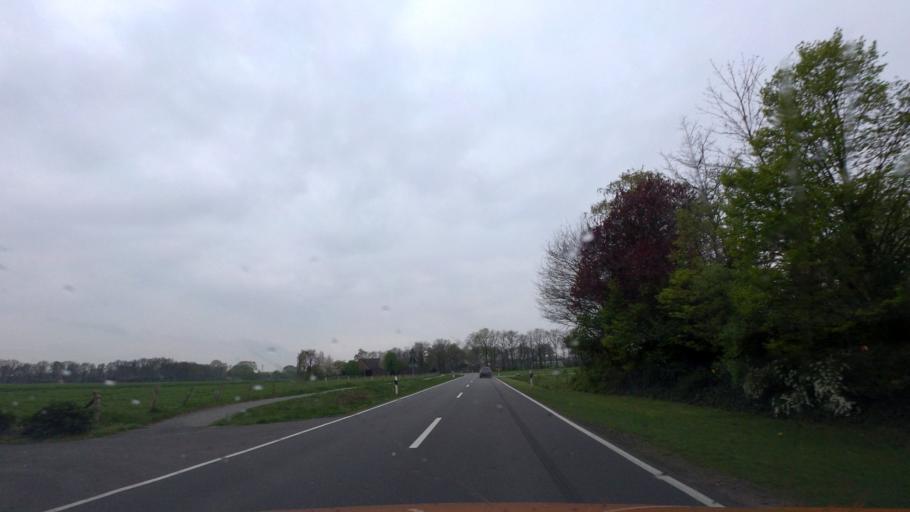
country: DE
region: Lower Saxony
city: Bakum
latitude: 52.7031
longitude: 8.1851
